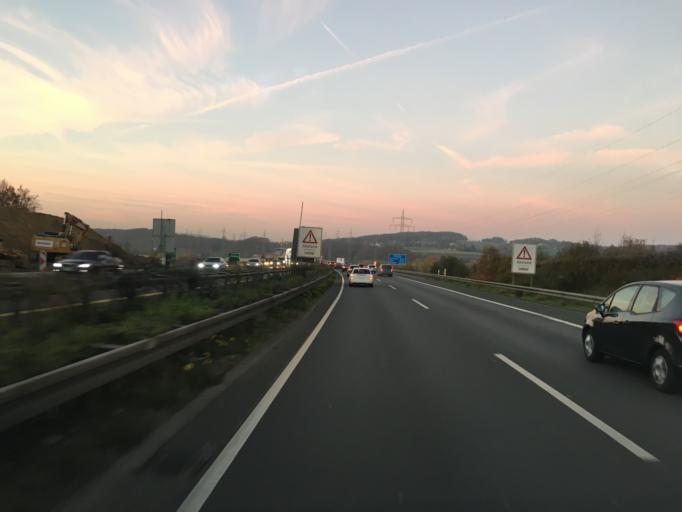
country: DE
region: North Rhine-Westphalia
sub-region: Regierungsbezirk Arnsberg
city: Hagen
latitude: 51.3764
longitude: 7.5239
